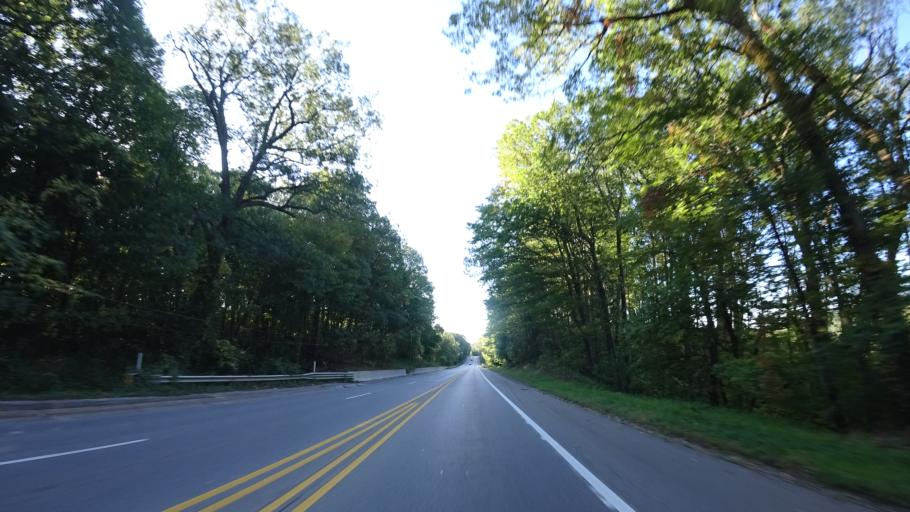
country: US
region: Michigan
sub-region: Kent County
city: Grandville
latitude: 42.9270
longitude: -85.7737
